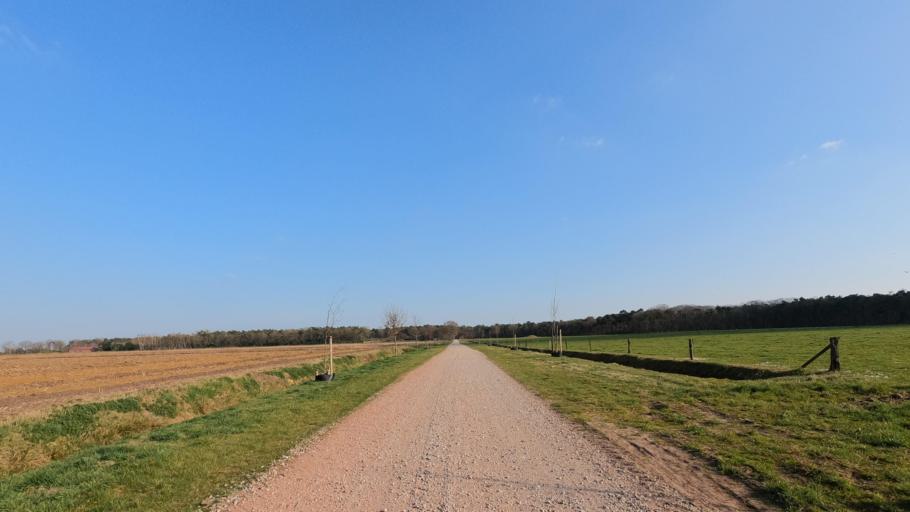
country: BE
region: Flanders
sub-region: Provincie Antwerpen
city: Baarle-Hertog
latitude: 51.3920
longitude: 4.8638
